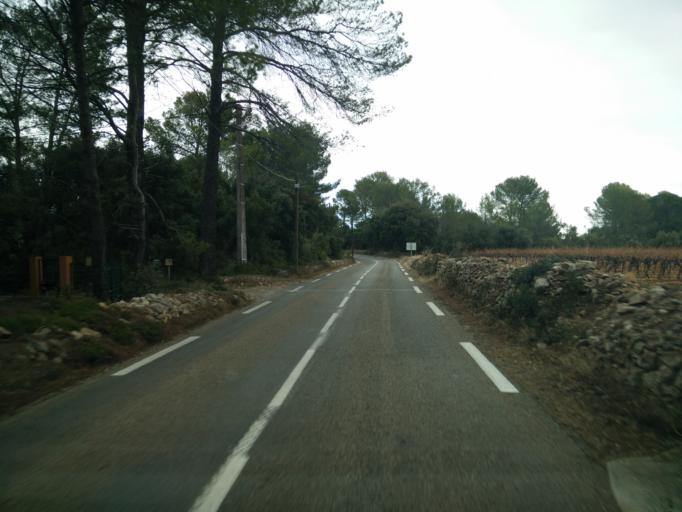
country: FR
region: Provence-Alpes-Cote d'Azur
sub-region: Departement du Var
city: Cotignac
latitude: 43.4903
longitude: 6.1398
